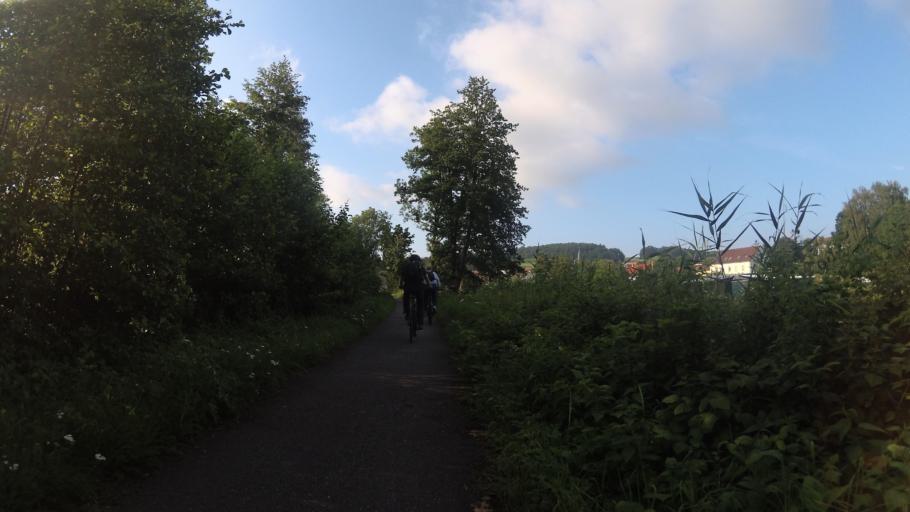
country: DE
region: Rheinland-Pfalz
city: Althornbach
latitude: 49.2011
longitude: 7.3739
